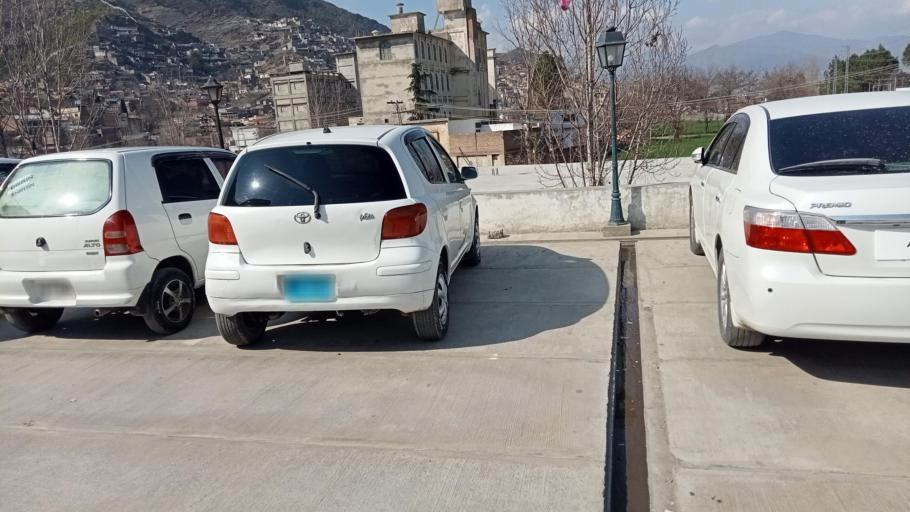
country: PK
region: Khyber Pakhtunkhwa
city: Saidu Sharif
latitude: 34.7540
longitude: 72.3554
